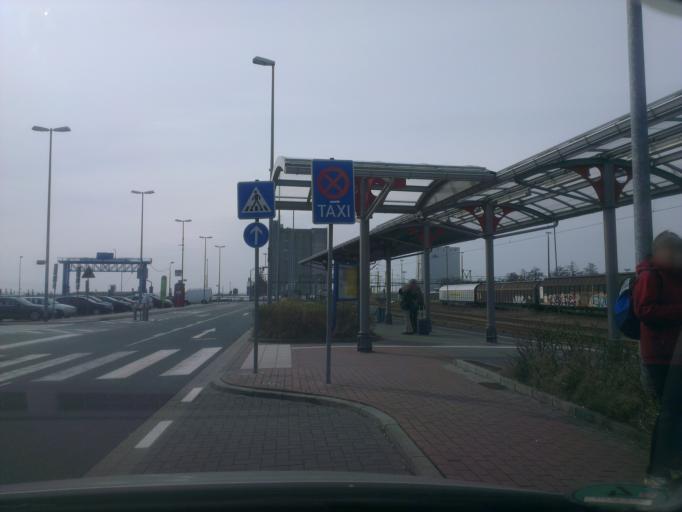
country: DE
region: Lower Saxony
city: Emden
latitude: 53.3436
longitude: 7.1859
